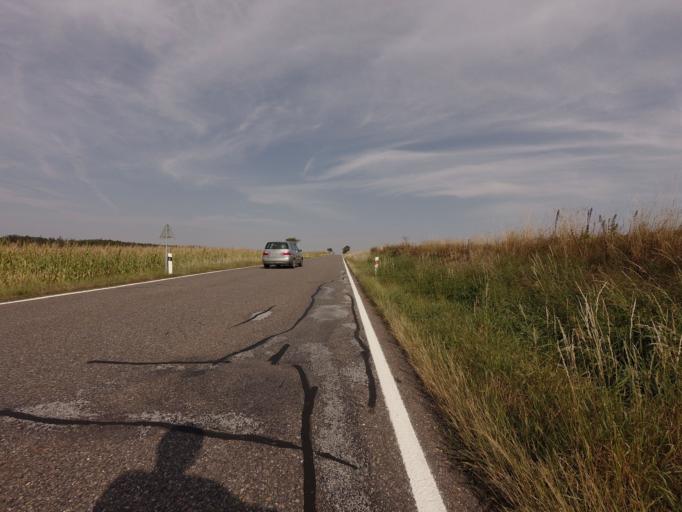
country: CZ
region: Central Bohemia
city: Petrovice
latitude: 49.5094
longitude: 14.3631
